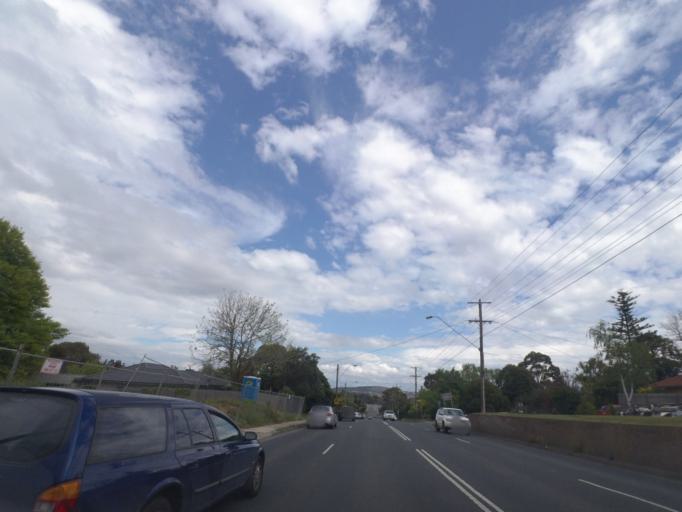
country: AU
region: Victoria
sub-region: Knox
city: Ferntree Gully
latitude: -37.8819
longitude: 145.2846
